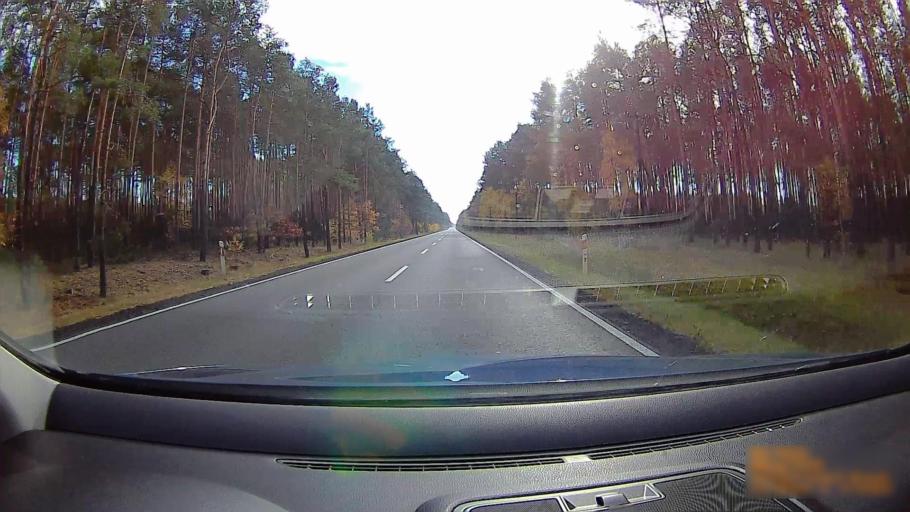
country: PL
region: Greater Poland Voivodeship
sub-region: Powiat ostrzeszowski
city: Ostrzeszow
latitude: 51.4716
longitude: 17.8921
